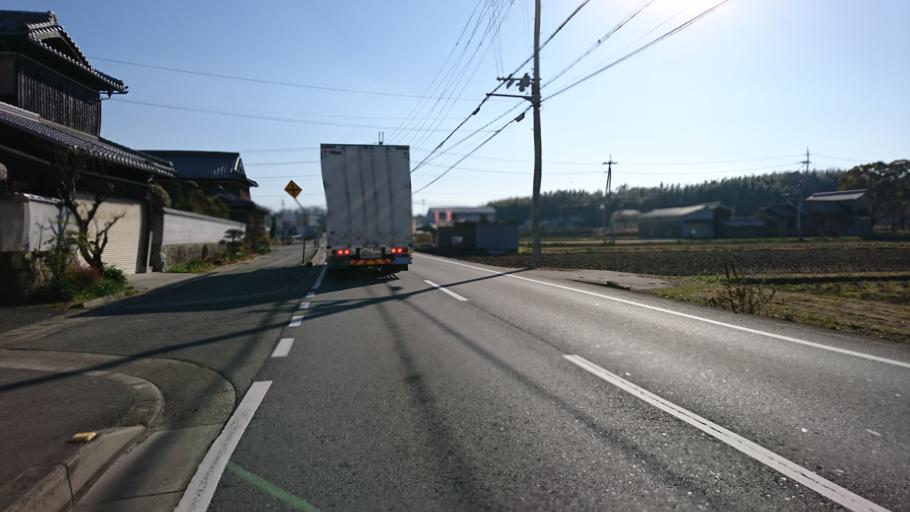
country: JP
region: Hyogo
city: Ono
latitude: 34.7881
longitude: 134.9010
